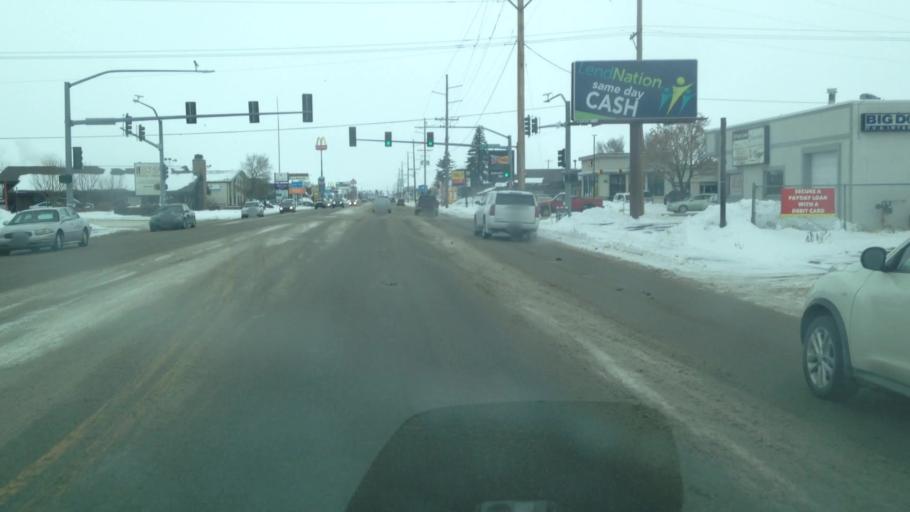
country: US
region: Idaho
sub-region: Madison County
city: Rexburg
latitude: 43.8297
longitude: -111.7781
